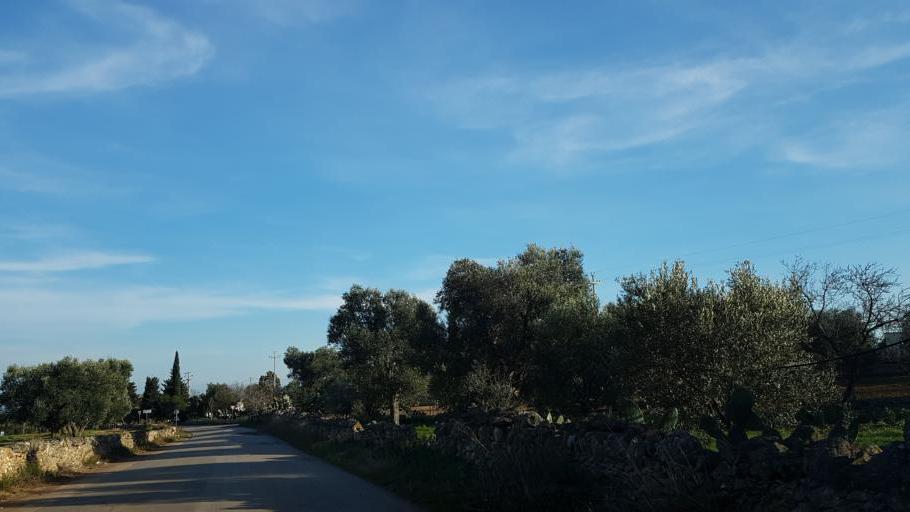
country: IT
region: Apulia
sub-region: Provincia di Brindisi
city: San Vito dei Normanni
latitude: 40.6973
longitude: 17.7406
